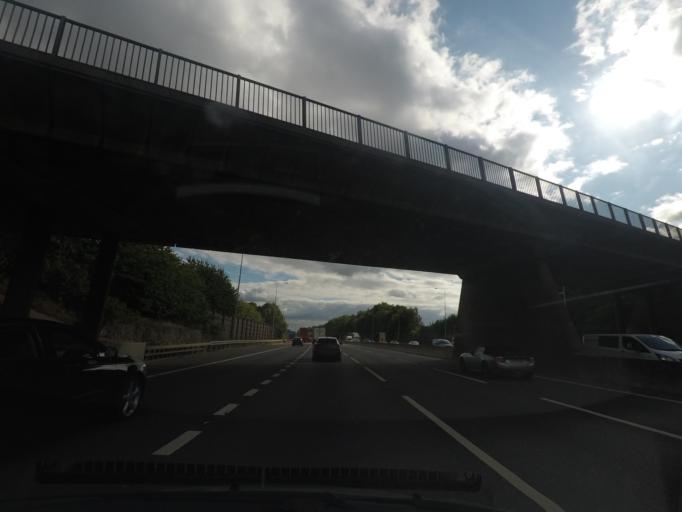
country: GB
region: England
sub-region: Derbyshire
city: Long Eaton
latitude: 52.9282
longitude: -1.3000
